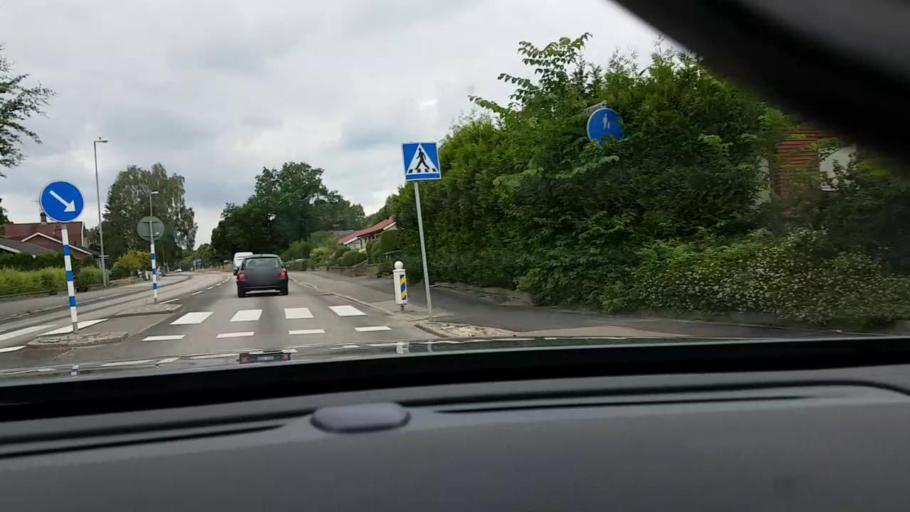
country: SE
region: Skane
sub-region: Hassleholms Kommun
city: Hassleholm
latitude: 56.1668
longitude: 13.7858
